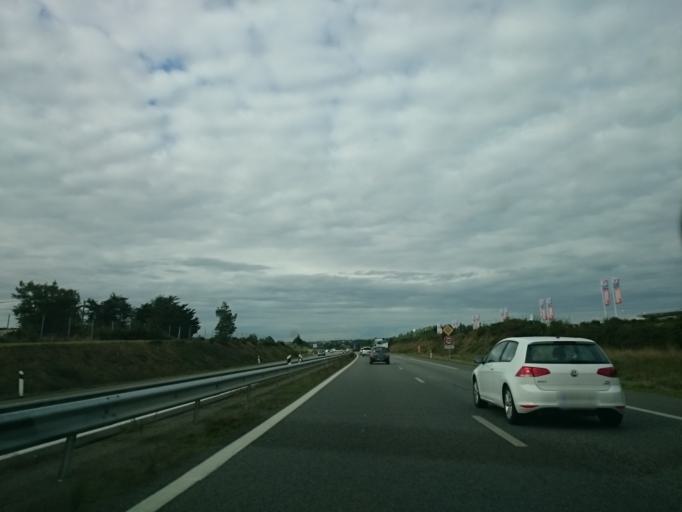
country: FR
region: Brittany
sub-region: Departement d'Ille-et-Vilaine
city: Bain-de-Bretagne
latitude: 47.8578
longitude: -1.6916
